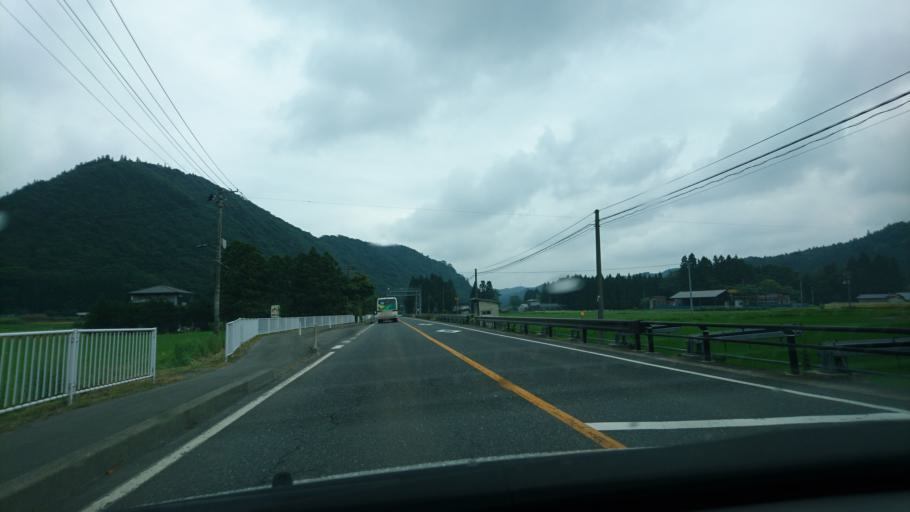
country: JP
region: Miyagi
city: Furukawa
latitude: 38.7267
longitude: 140.7972
